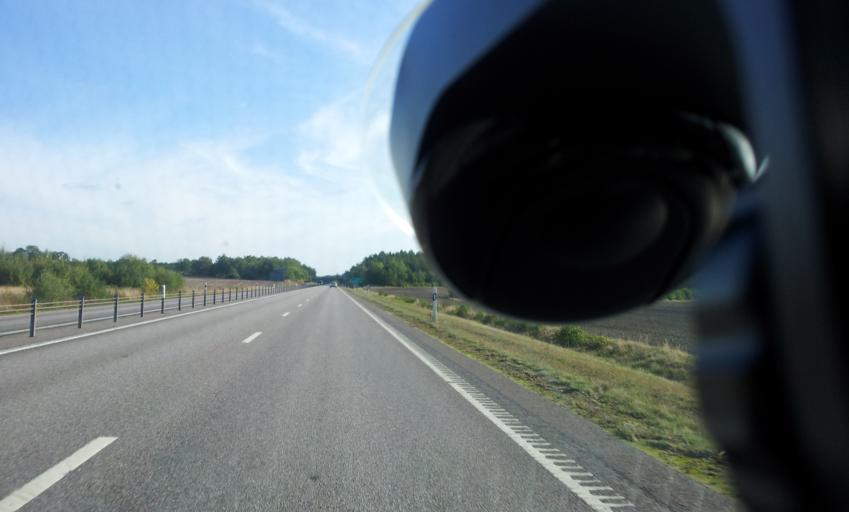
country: SE
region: Kalmar
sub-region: Kalmar Kommun
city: Ljungbyholm
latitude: 56.6254
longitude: 16.1813
